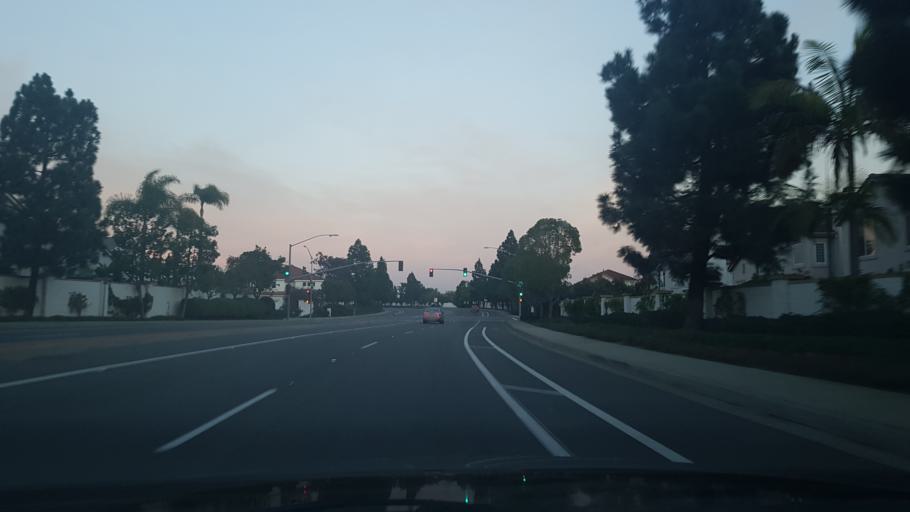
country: US
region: California
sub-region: San Diego County
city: Fairbanks Ranch
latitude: 32.9178
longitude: -117.1867
